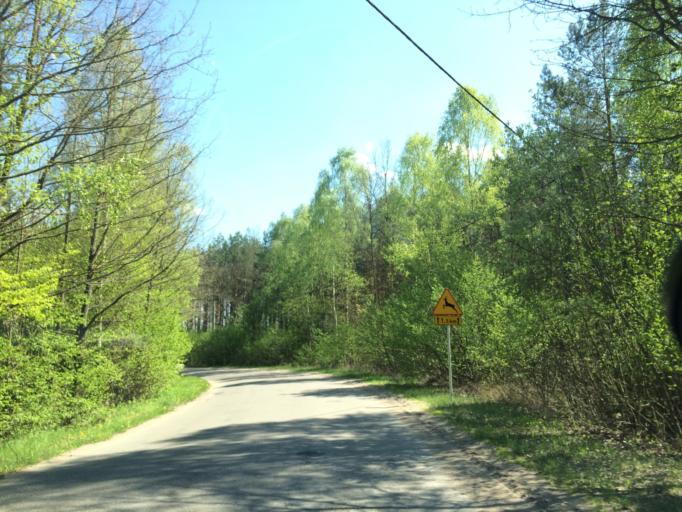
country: PL
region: Warmian-Masurian Voivodeship
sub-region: Powiat nowomiejski
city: Kurzetnik
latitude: 53.3701
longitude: 19.5212
